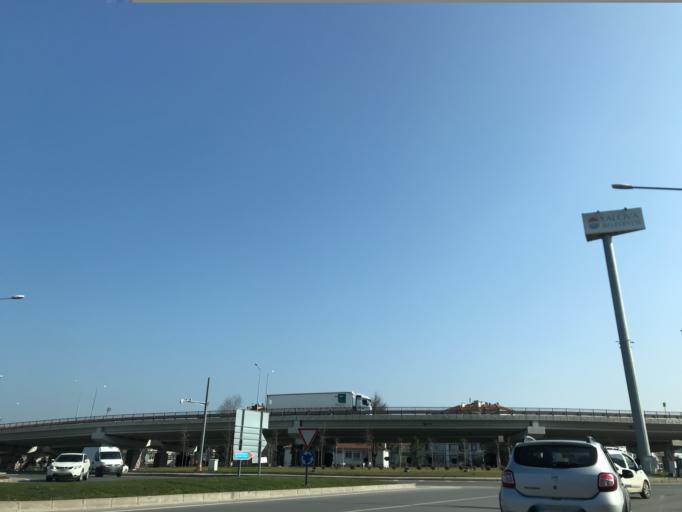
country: TR
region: Yalova
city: Yalova
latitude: 40.6569
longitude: 29.2830
